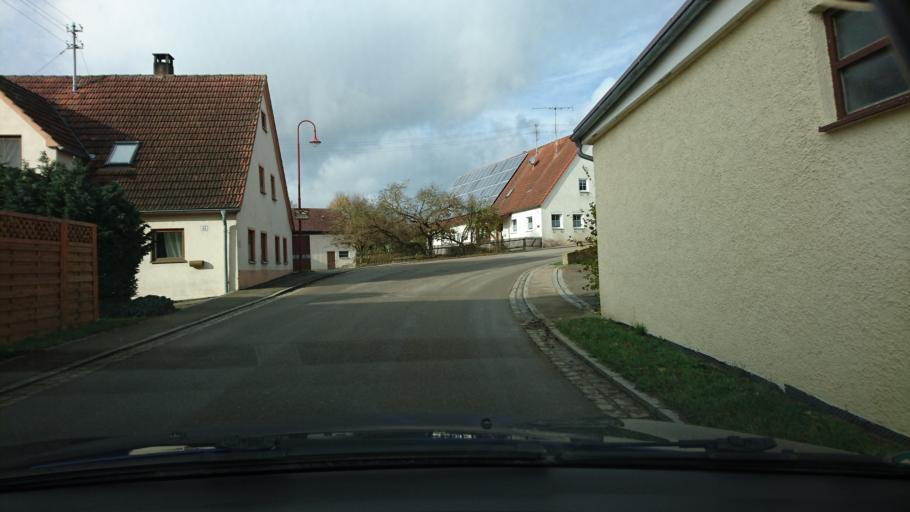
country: DE
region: Bavaria
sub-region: Swabia
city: Amerdingen
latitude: 48.7488
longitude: 10.4675
